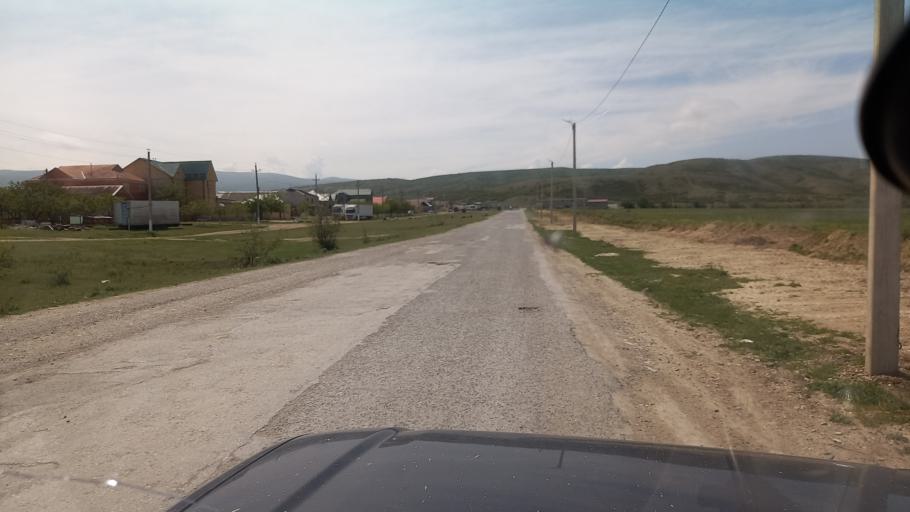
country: RU
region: Dagestan
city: Gurbuki
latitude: 42.6174
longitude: 47.5912
